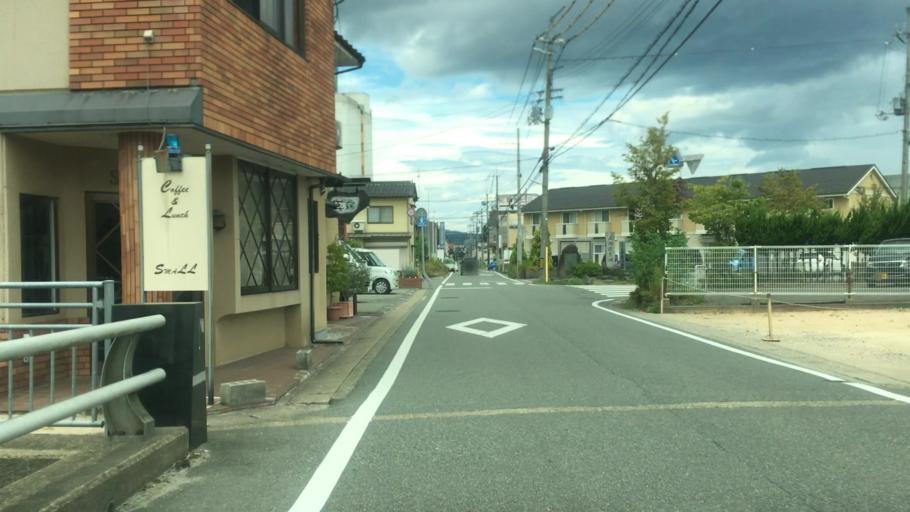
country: JP
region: Hyogo
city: Toyooka
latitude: 35.5319
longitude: 134.8210
